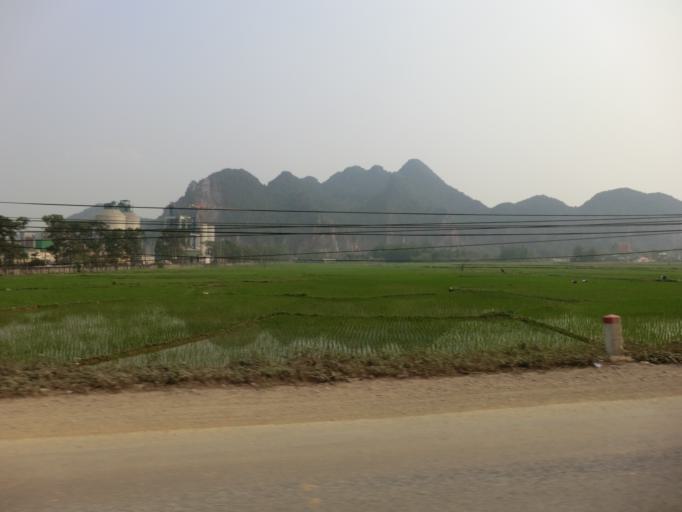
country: VN
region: Hoa Binh
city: Luong Son
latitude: 20.8561
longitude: 105.5881
